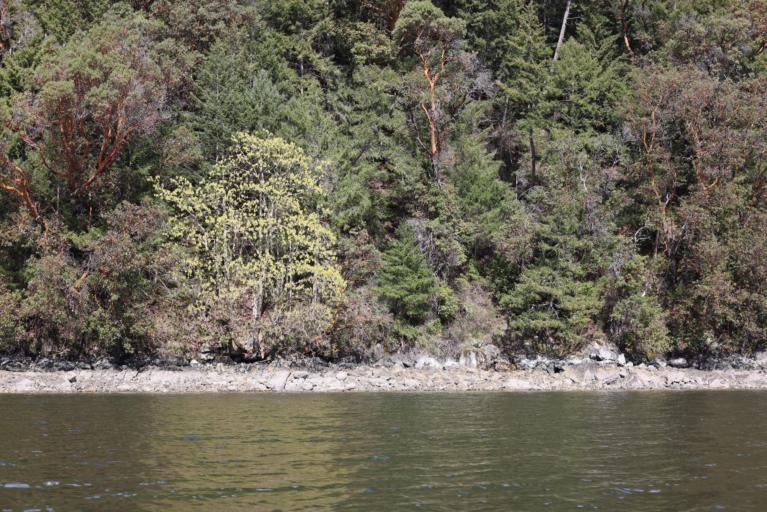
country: CA
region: British Columbia
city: Langford
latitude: 48.5583
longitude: -123.5373
